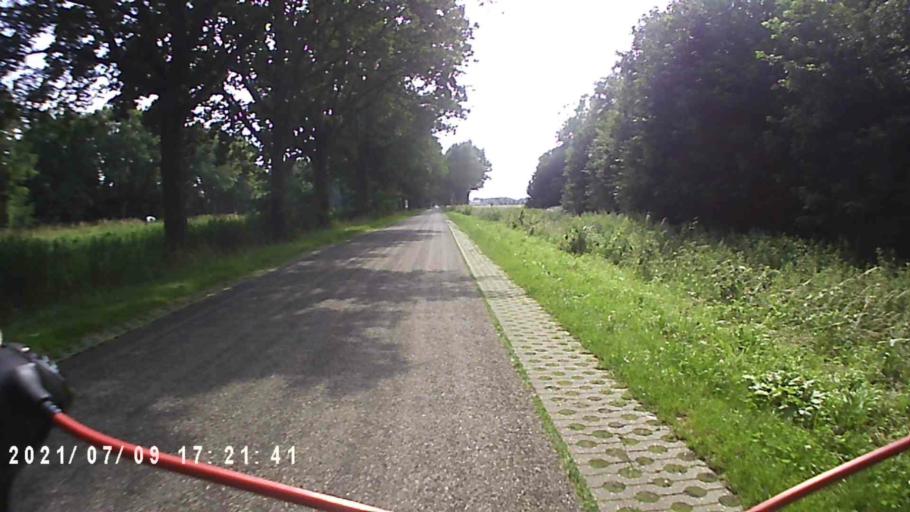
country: NL
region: Groningen
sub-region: Gemeente Vlagtwedde
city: Vlagtwedde
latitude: 53.0830
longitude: 7.1591
